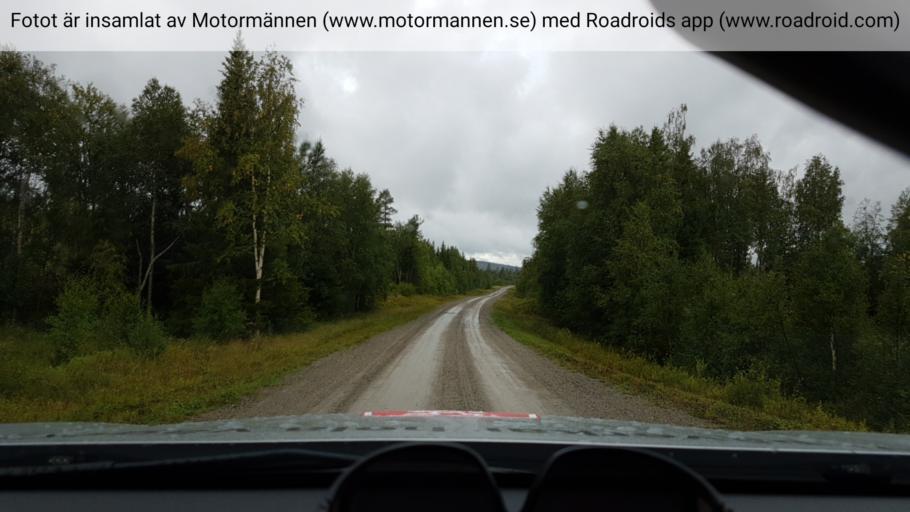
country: SE
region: Vaesterbotten
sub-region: Asele Kommun
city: Insjon
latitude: 64.7854
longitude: 17.5882
